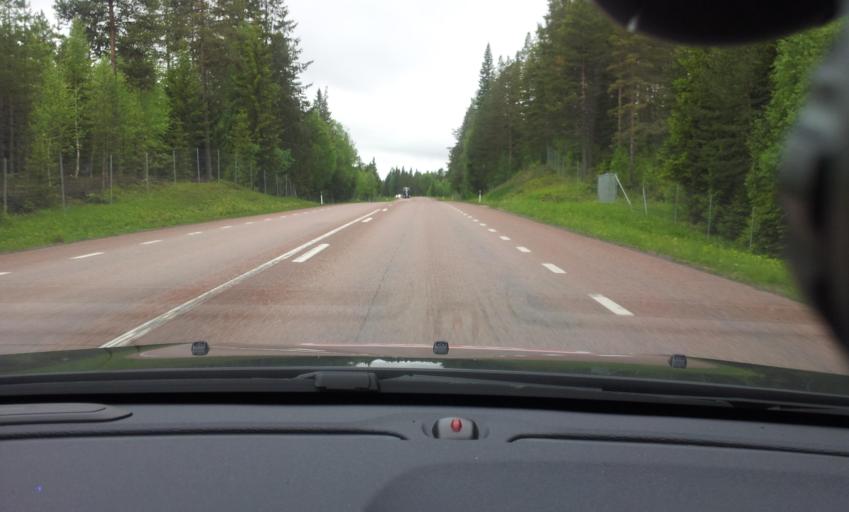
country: SE
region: Jaemtland
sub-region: Krokoms Kommun
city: Krokom
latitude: 63.3264
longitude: 14.3668
